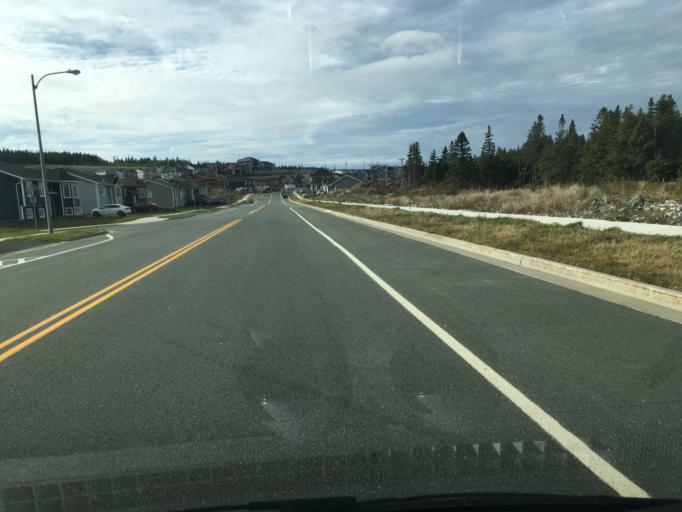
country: CA
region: Newfoundland and Labrador
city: Mount Pearl
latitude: 47.5550
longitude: -52.7940
